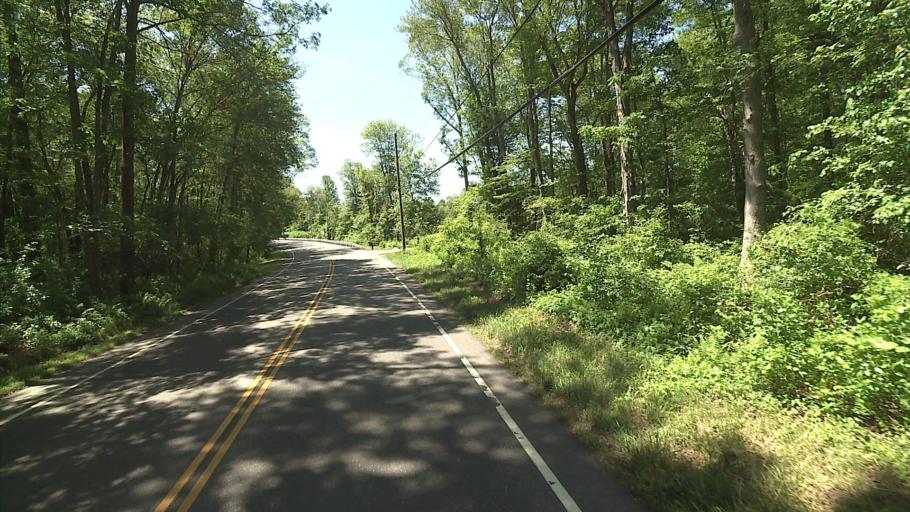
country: US
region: Rhode Island
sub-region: Washington County
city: Hopkinton
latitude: 41.4790
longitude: -71.8318
